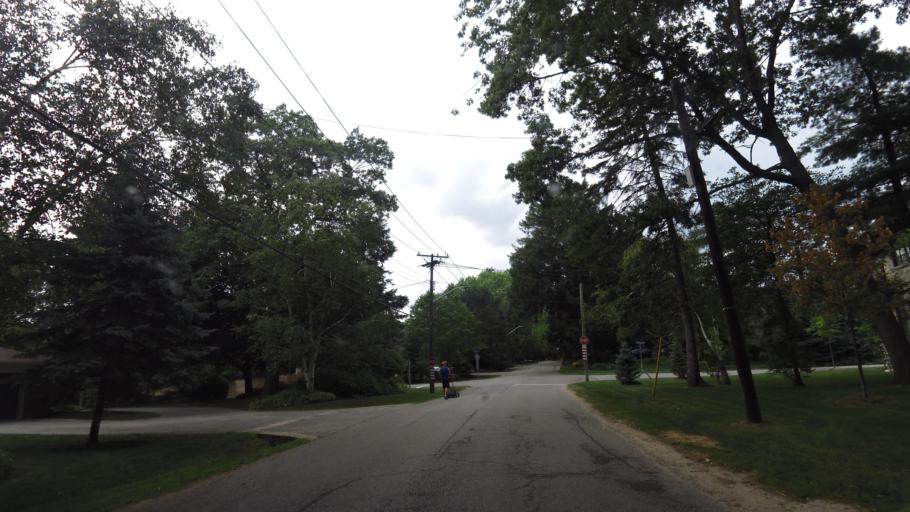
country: CA
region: Ontario
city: Mississauga
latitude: 43.5564
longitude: -79.6033
